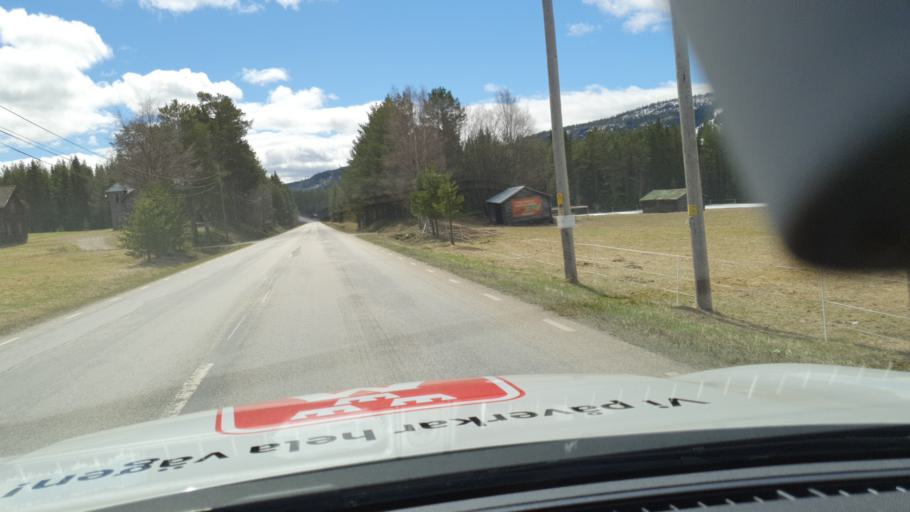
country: SE
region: Jaemtland
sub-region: Bergs Kommun
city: Hoverberg
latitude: 62.5156
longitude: 14.1944
